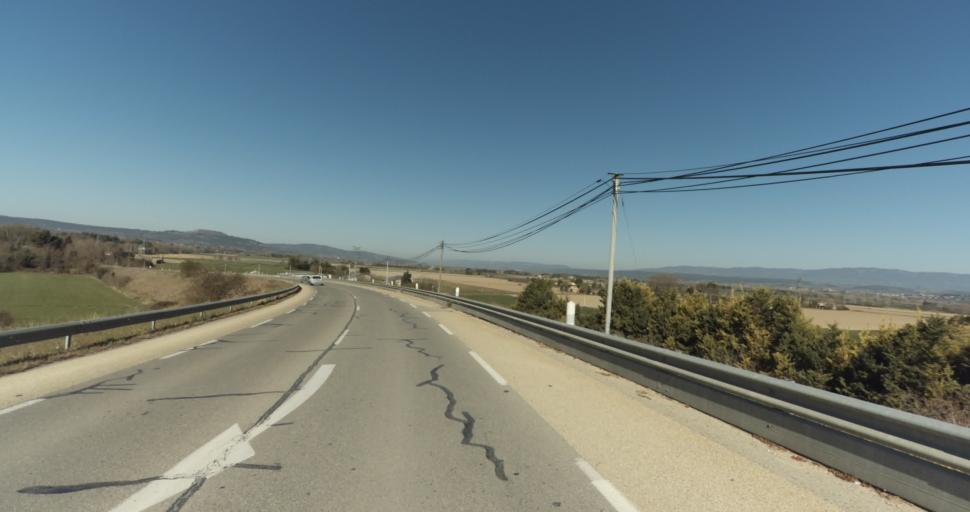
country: FR
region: Provence-Alpes-Cote d'Azur
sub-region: Departement des Bouches-du-Rhone
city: Meyrargues
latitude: 43.6449
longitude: 5.5227
